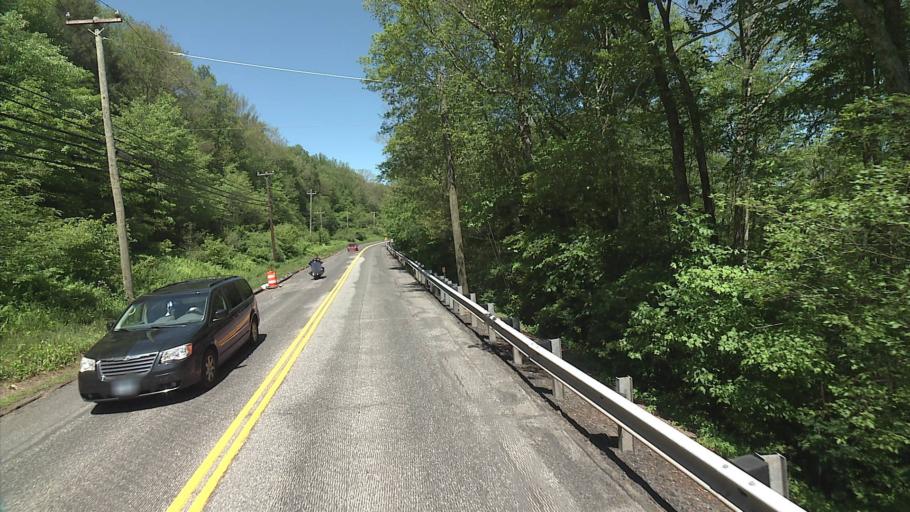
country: US
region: Connecticut
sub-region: Middlesex County
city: East Hampton
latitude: 41.5614
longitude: -72.4595
